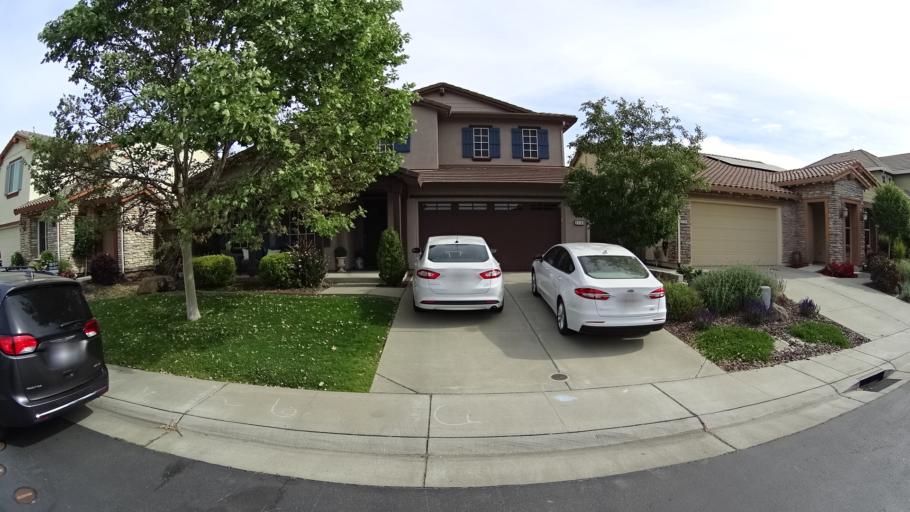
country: US
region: California
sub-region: Placer County
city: Lincoln
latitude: 38.8362
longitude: -121.2756
